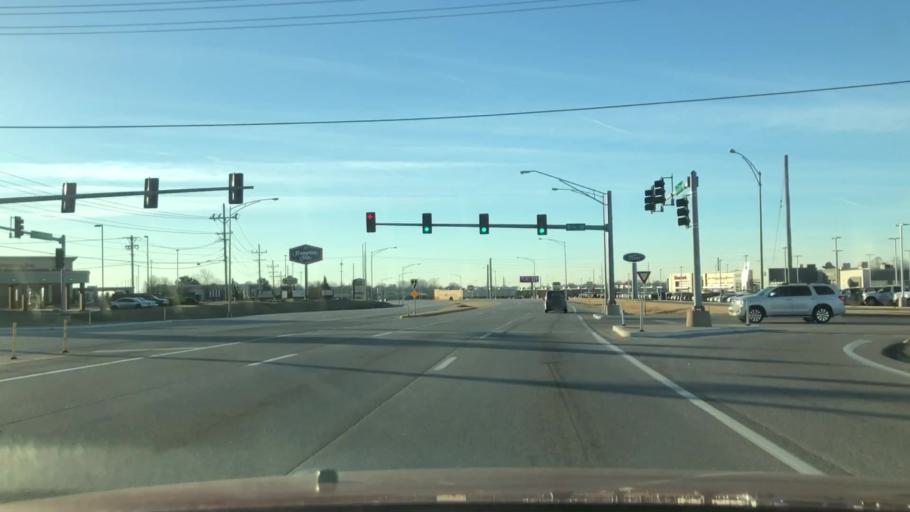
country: US
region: Missouri
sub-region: Greene County
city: Springfield
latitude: 37.1567
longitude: -93.2629
